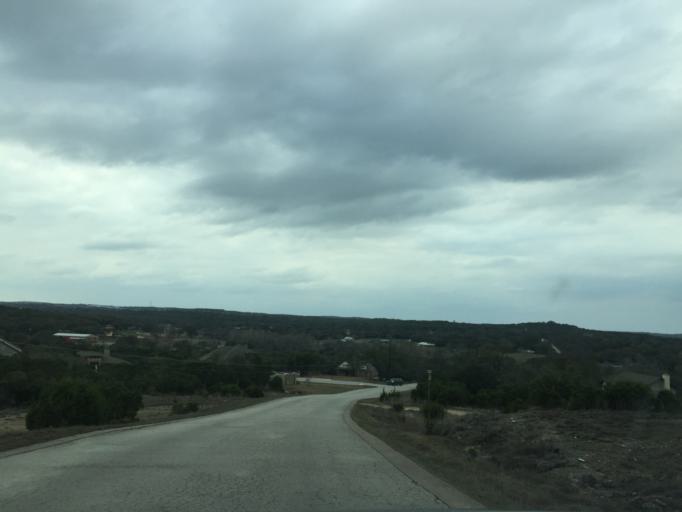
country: US
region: Texas
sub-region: Travis County
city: Shady Hollow
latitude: 30.1475
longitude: -97.9718
